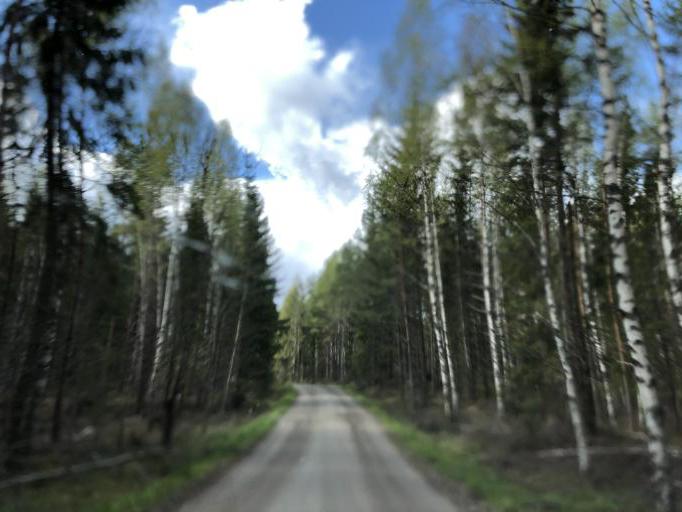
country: SE
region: Uppsala
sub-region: Heby Kommun
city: Tarnsjo
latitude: 60.2563
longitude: 16.9104
